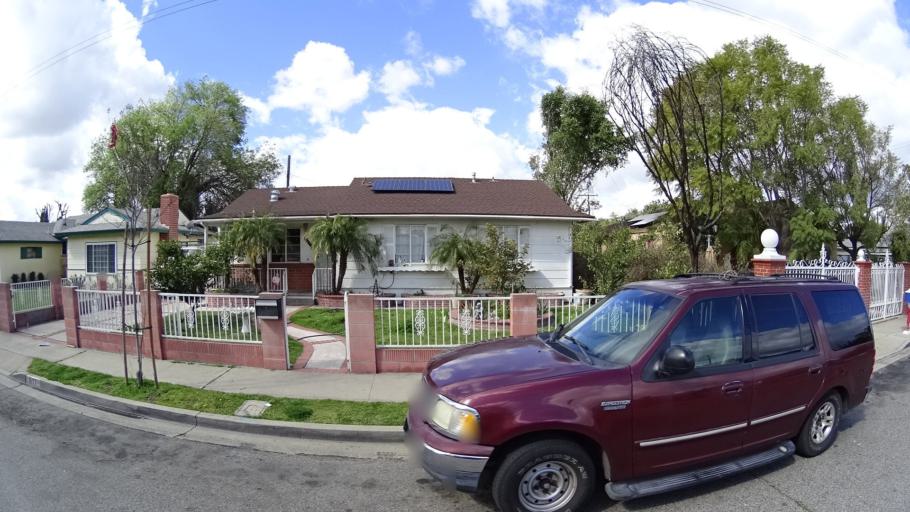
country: US
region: California
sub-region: Orange County
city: Anaheim
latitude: 33.8445
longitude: -117.9015
